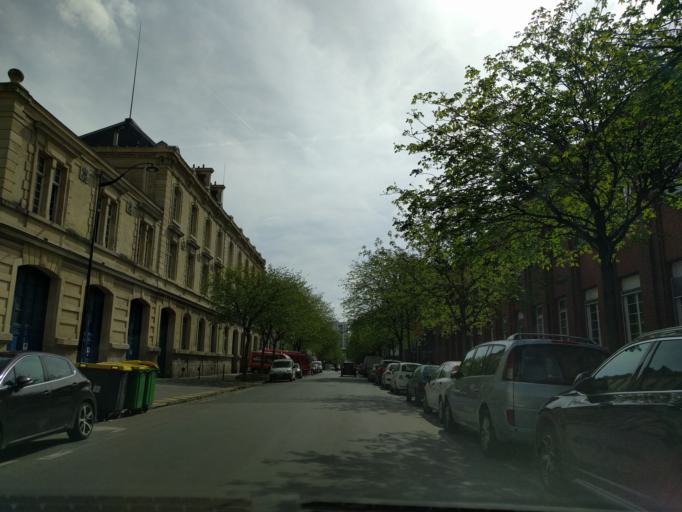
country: FR
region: Ile-de-France
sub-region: Departement du Val-de-Marne
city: Ivry-sur-Seine
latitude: 48.8480
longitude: 2.3840
